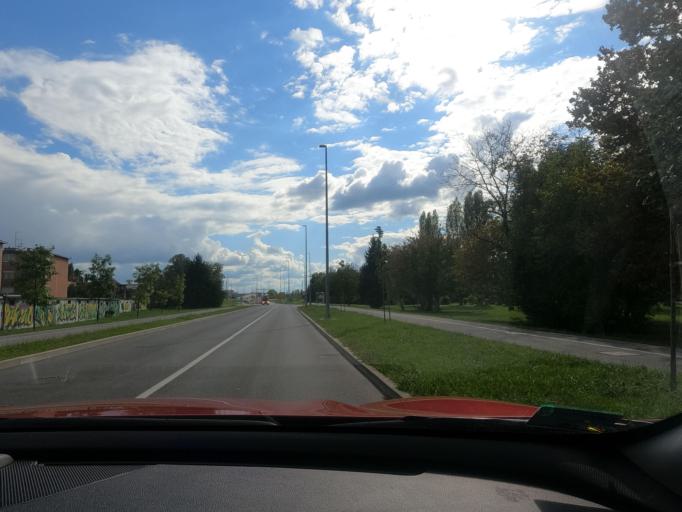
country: HR
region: Sisacko-Moslavacka
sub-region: Grad Sisak
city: Sisak
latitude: 45.4981
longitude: 16.3695
